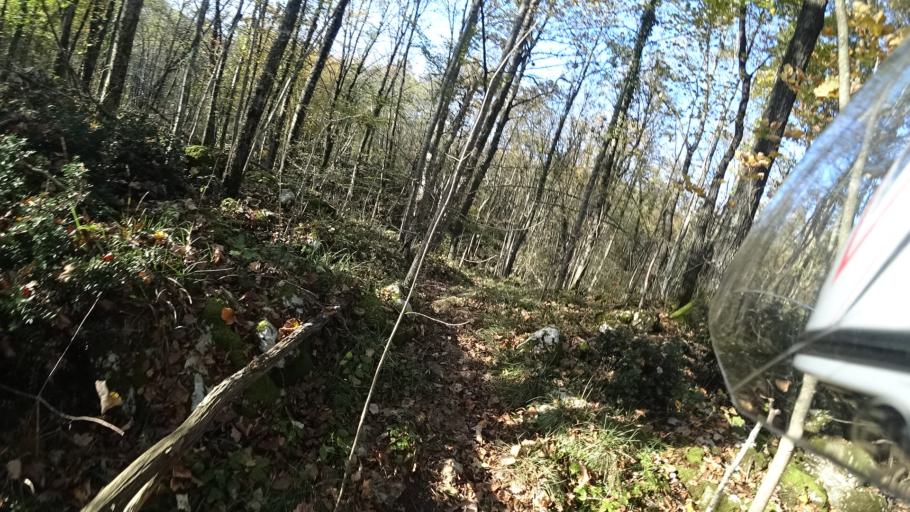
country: HR
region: Primorsko-Goranska
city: Matulji
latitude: 45.3876
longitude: 14.2967
